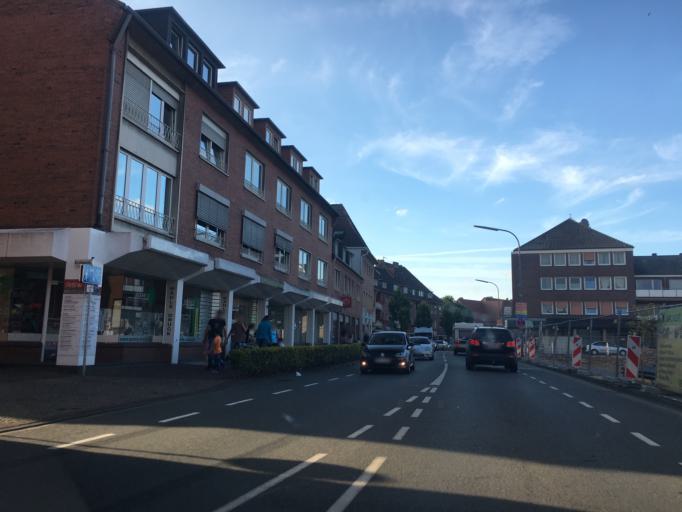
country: DE
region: North Rhine-Westphalia
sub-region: Regierungsbezirk Munster
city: Dulmen
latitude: 51.8290
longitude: 7.2794
